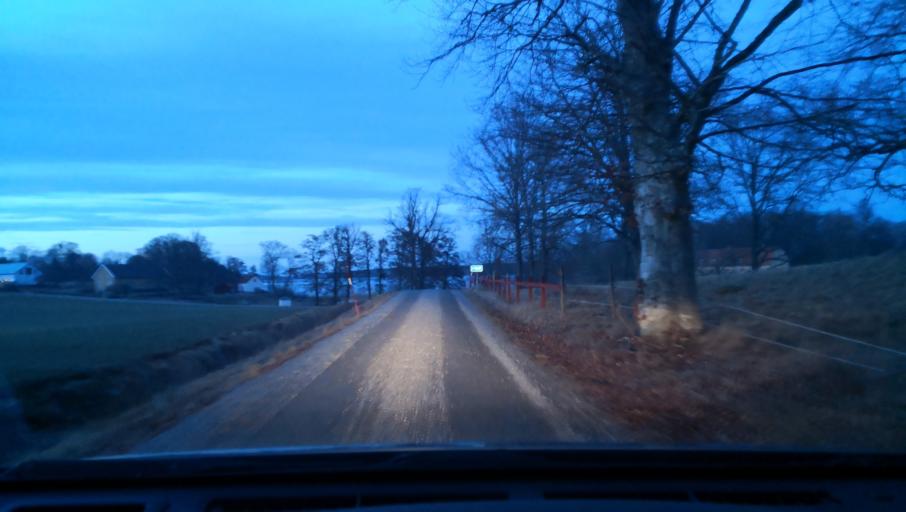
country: SE
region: Uppsala
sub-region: Enkopings Kommun
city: Dalby
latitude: 59.5718
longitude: 17.3789
